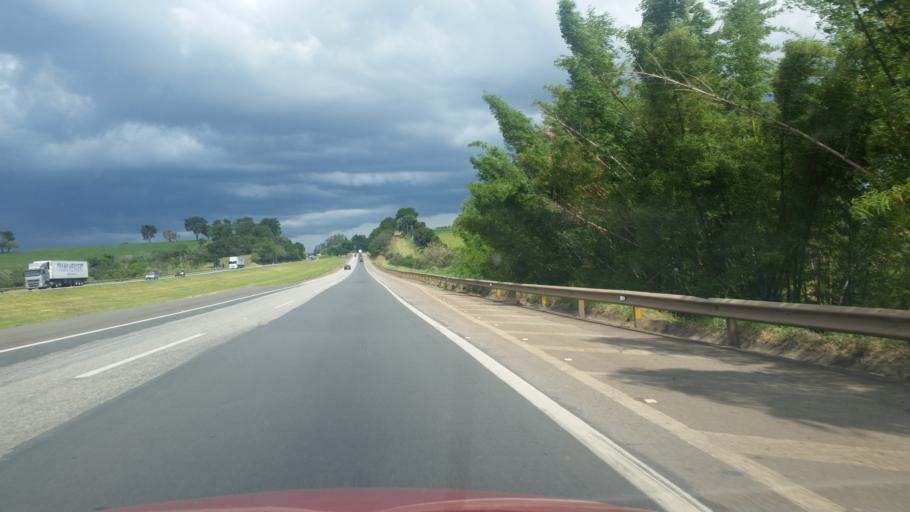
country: BR
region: Sao Paulo
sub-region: Boituva
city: Boituva
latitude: -23.2950
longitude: -47.7191
